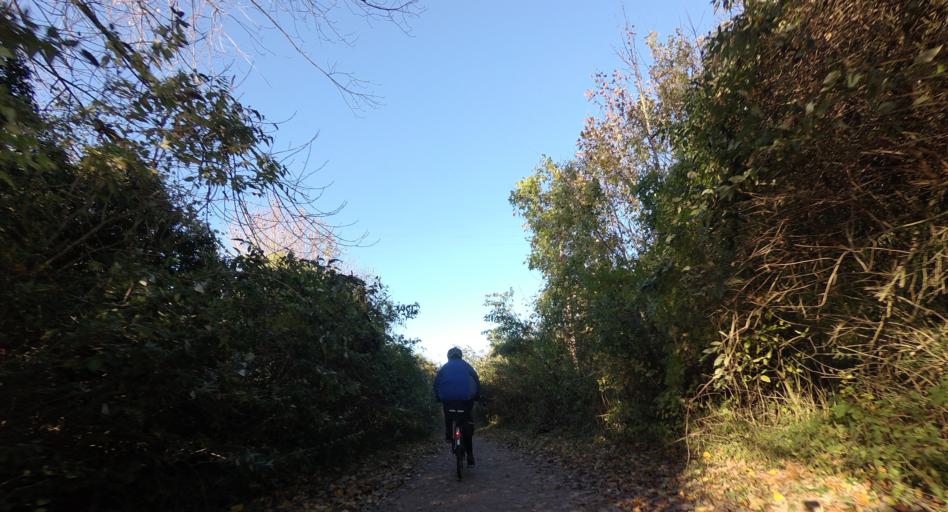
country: GB
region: England
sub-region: West Sussex
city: Steyning
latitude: 50.8661
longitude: -0.2981
